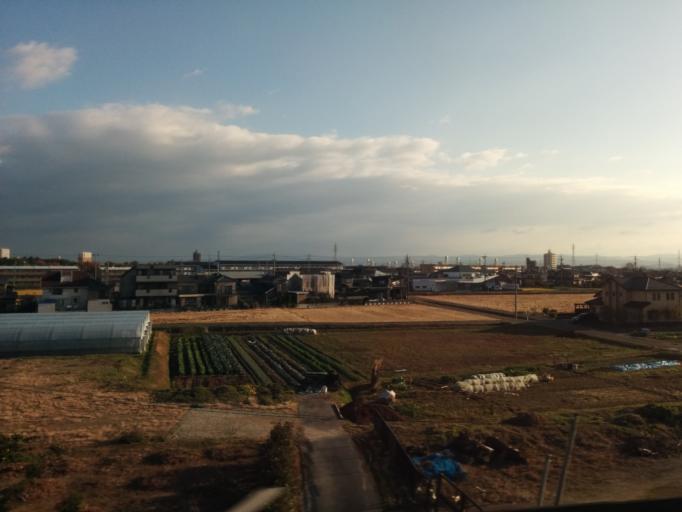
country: JP
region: Aichi
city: Anjo
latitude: 34.9449
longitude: 137.0826
